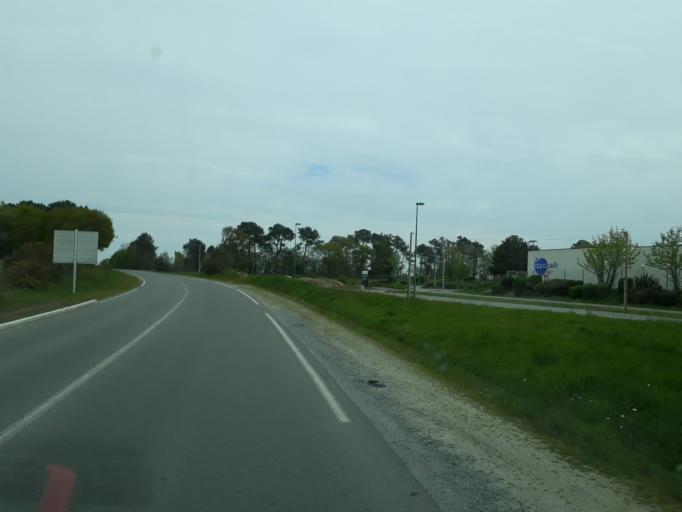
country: FR
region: Brittany
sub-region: Departement du Morbihan
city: Surzur
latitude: 47.5927
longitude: -2.6244
